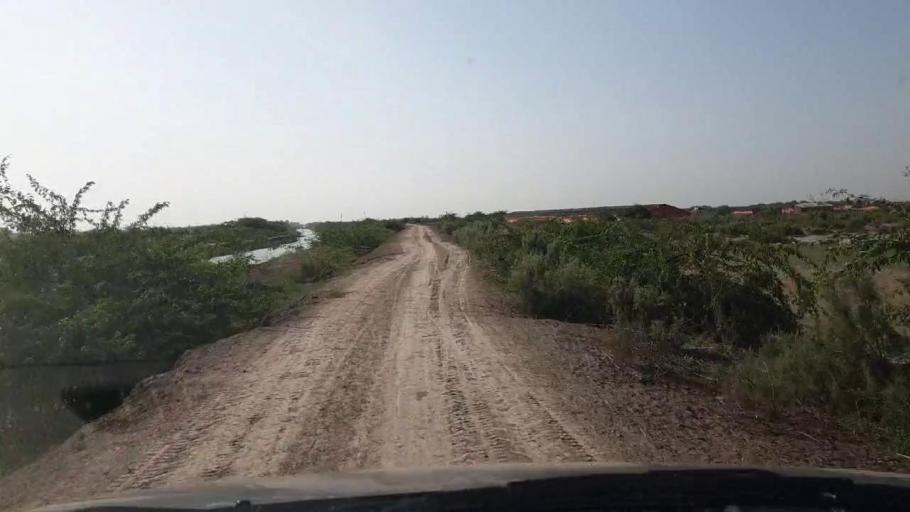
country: PK
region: Sindh
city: Kadhan
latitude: 24.6122
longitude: 69.0730
